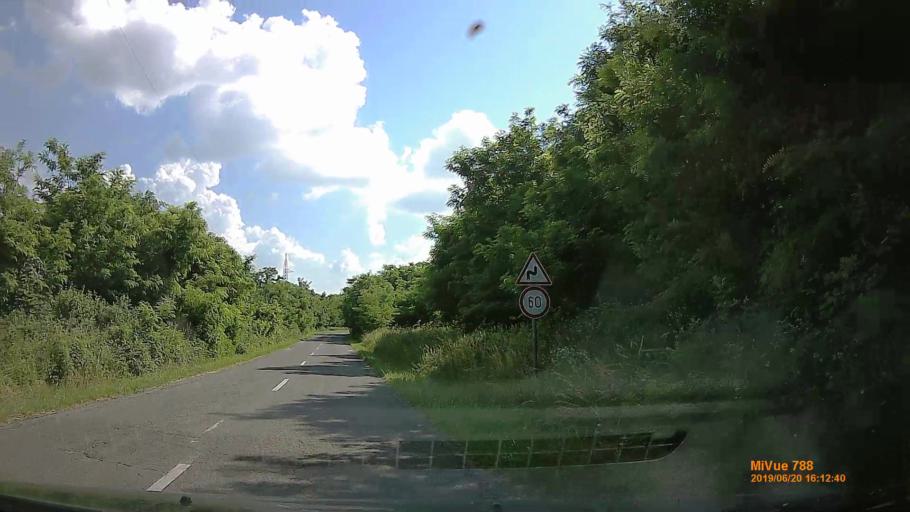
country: HU
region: Baranya
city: Pellerd
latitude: 46.1000
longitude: 18.0934
